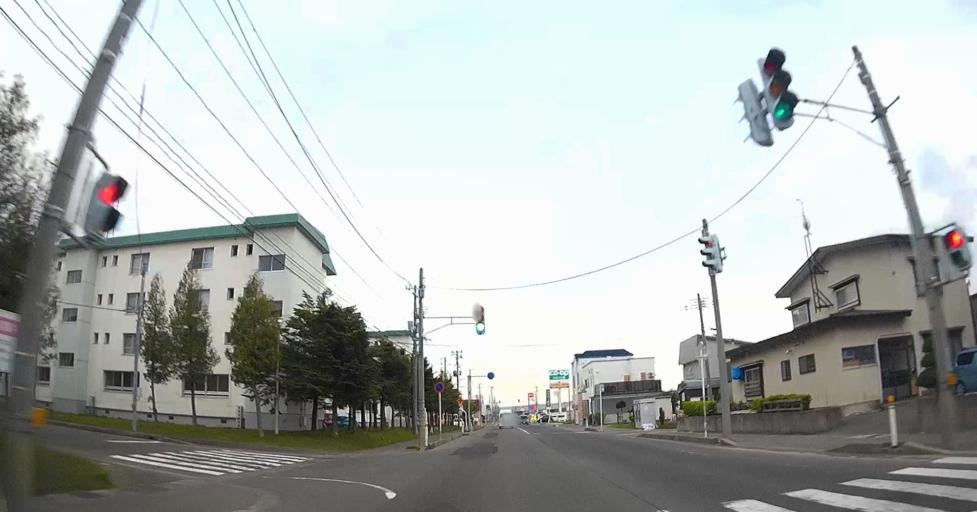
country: JP
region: Aomori
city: Aomori Shi
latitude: 40.8579
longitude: 140.6813
